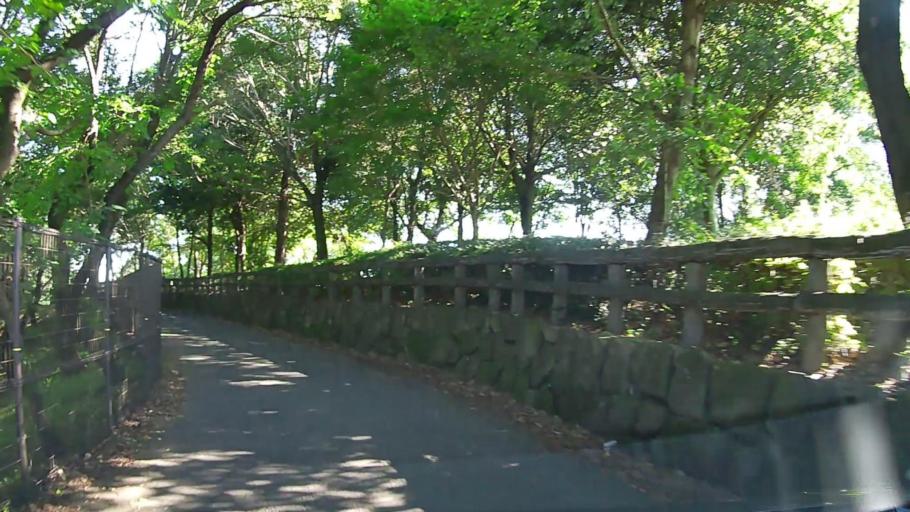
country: JP
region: Tokyo
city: Fussa
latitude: 35.7763
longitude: 139.3628
